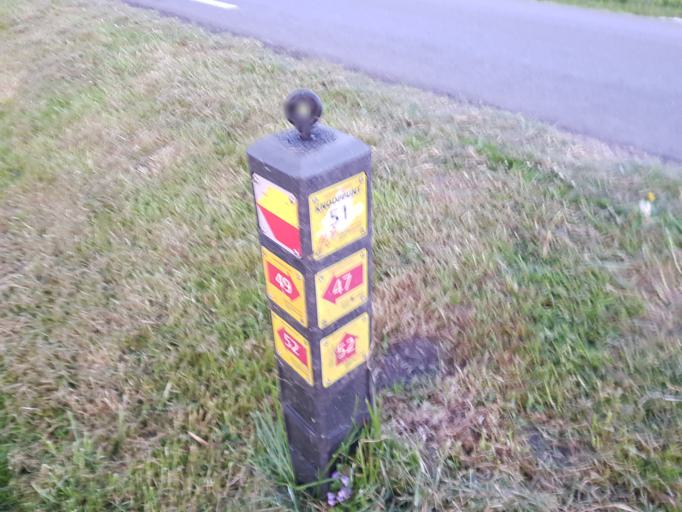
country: NL
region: South Holland
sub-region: Gemeente Gouda
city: Gouda
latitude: 51.9517
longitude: 4.7182
